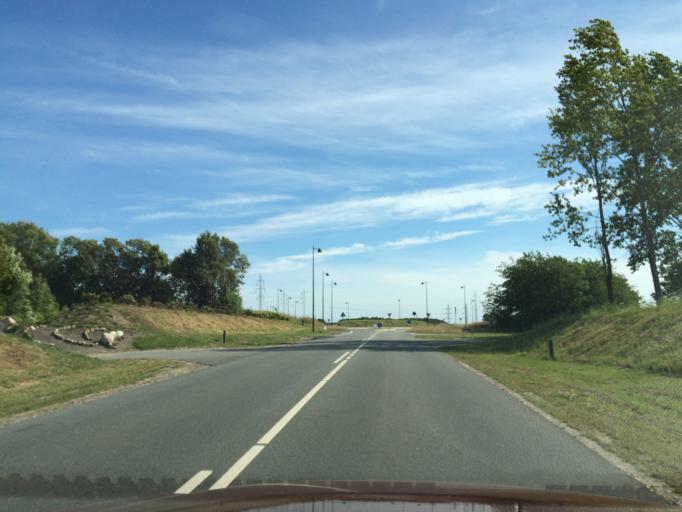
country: DK
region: Central Jutland
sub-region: Silkeborg Kommune
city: Silkeborg
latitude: 56.2093
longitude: 9.5621
